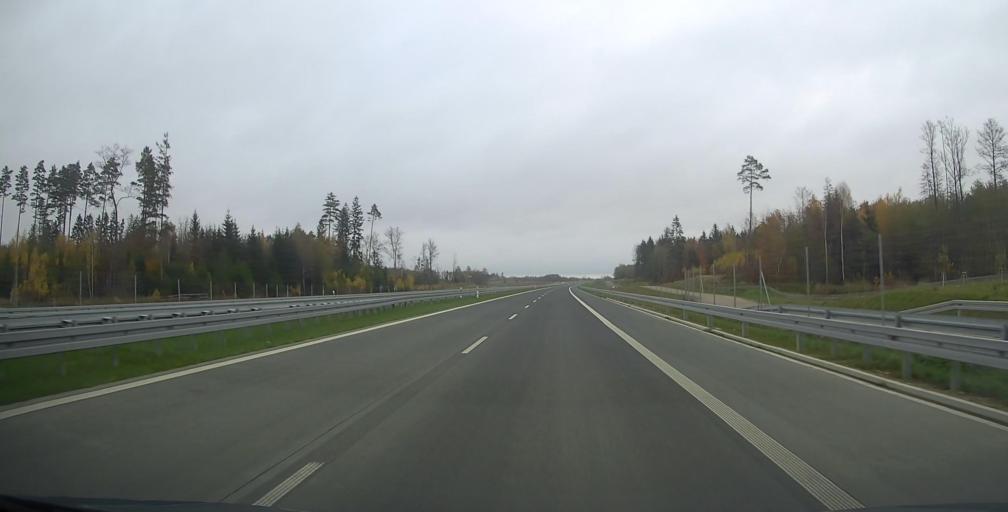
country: PL
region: Podlasie
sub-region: Powiat suwalski
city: Raczki
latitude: 53.8993
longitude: 22.6926
